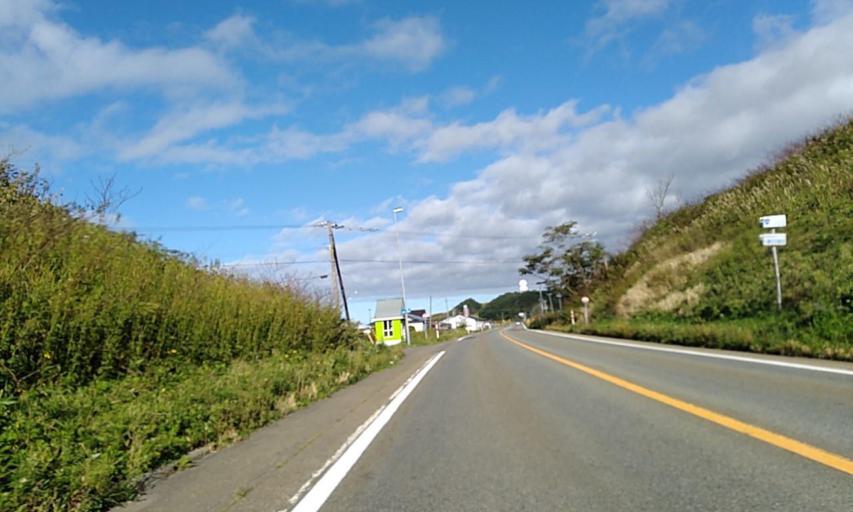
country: JP
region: Hokkaido
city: Shizunai-furukawacho
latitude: 42.2271
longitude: 142.6188
